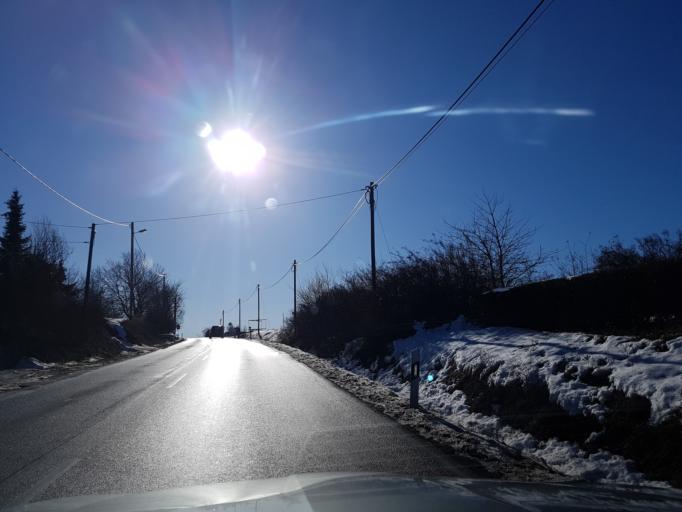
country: DE
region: Saxony
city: Radebeul
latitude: 51.1224
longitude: 13.6887
